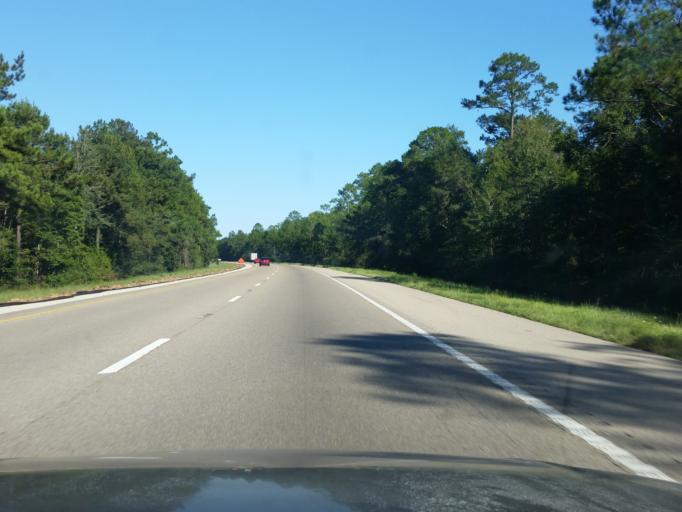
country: US
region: Mississippi
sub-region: Hancock County
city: Pearlington
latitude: 30.3317
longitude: -89.5326
